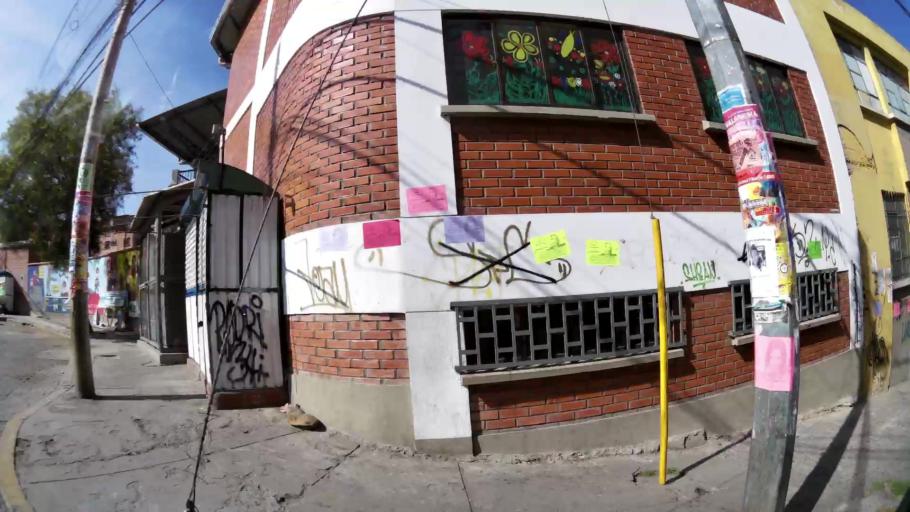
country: BO
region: La Paz
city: La Paz
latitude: -16.4978
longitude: -68.1158
